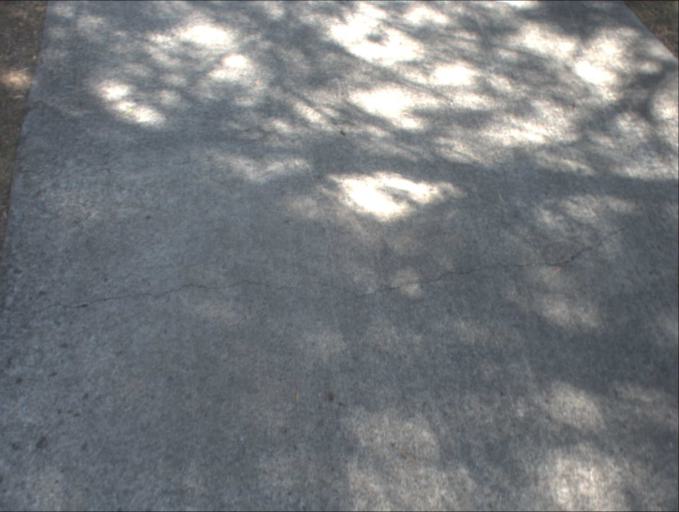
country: AU
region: Queensland
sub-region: Logan
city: Beenleigh
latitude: -27.6813
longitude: 153.1799
